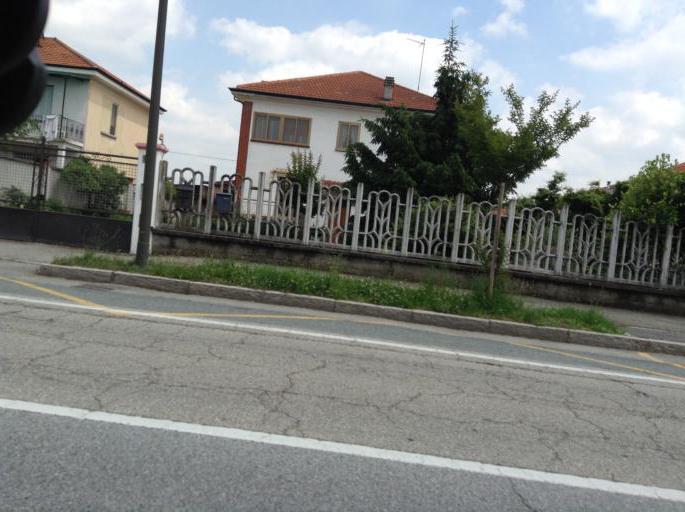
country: IT
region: Piedmont
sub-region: Provincia di Torino
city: Carignano
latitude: 44.8982
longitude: 7.6704
